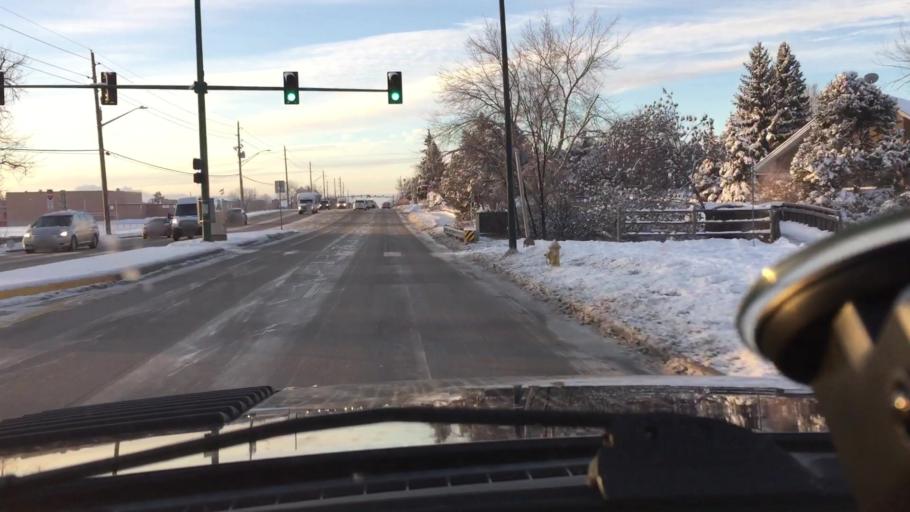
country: US
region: Colorado
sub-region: Adams County
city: Northglenn
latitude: 39.8970
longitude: -104.9968
